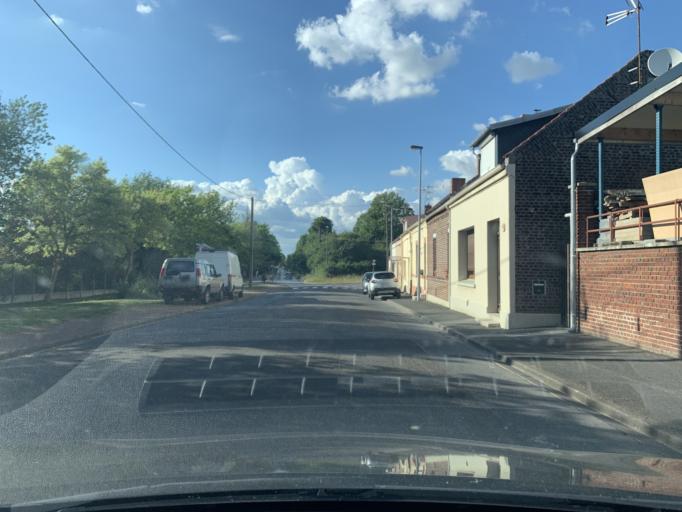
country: FR
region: Nord-Pas-de-Calais
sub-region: Departement du Nord
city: Cambrai
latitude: 50.1727
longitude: 3.2579
